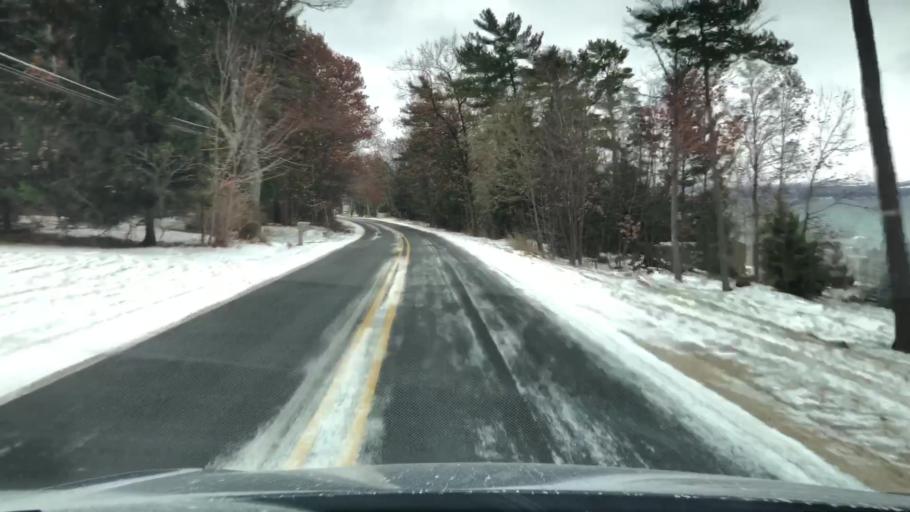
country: US
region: Michigan
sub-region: Grand Traverse County
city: Traverse City
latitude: 44.8240
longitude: -85.5697
